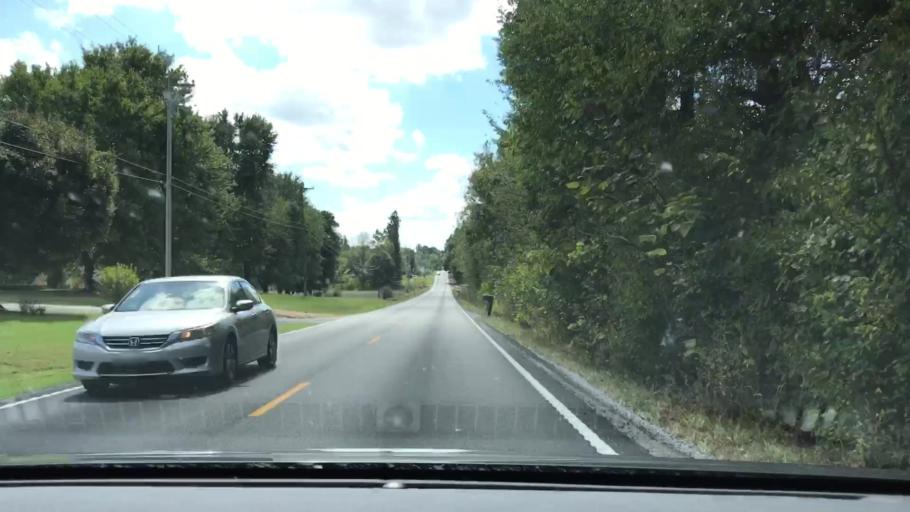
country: US
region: Kentucky
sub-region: Graves County
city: Mayfield
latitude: 36.7874
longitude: -88.5957
